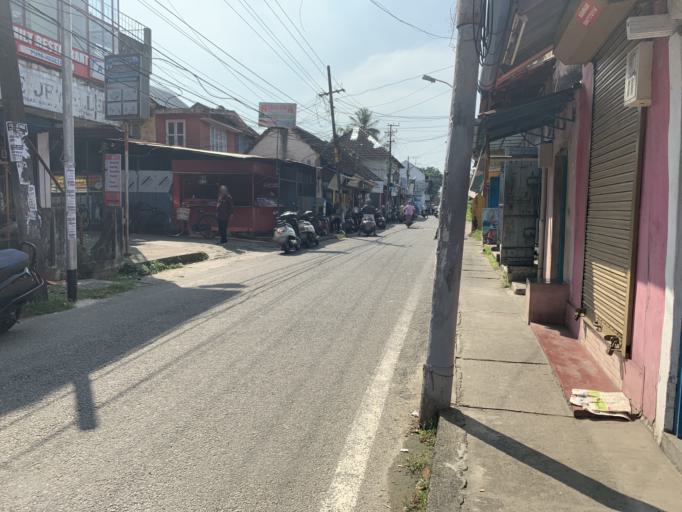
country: IN
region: Kerala
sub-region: Ernakulam
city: Cochin
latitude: 9.9578
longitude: 76.2563
